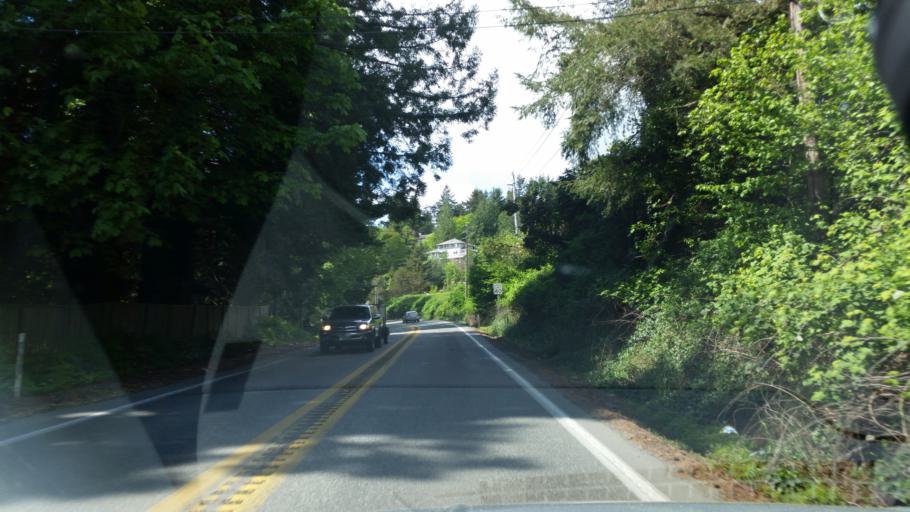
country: US
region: Washington
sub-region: Pierce County
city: Wauna
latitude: 47.3786
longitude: -122.6456
